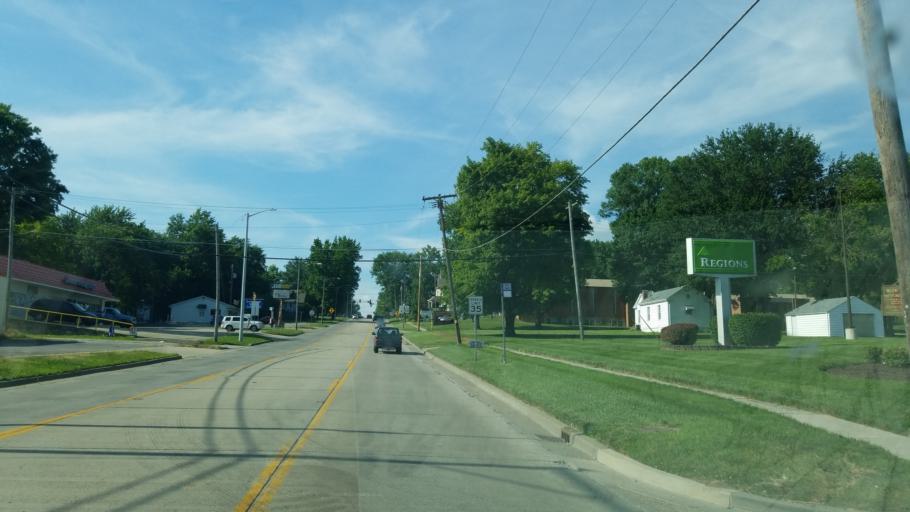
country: US
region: Illinois
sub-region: Saint Clair County
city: Lebanon
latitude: 38.6011
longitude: -89.8076
